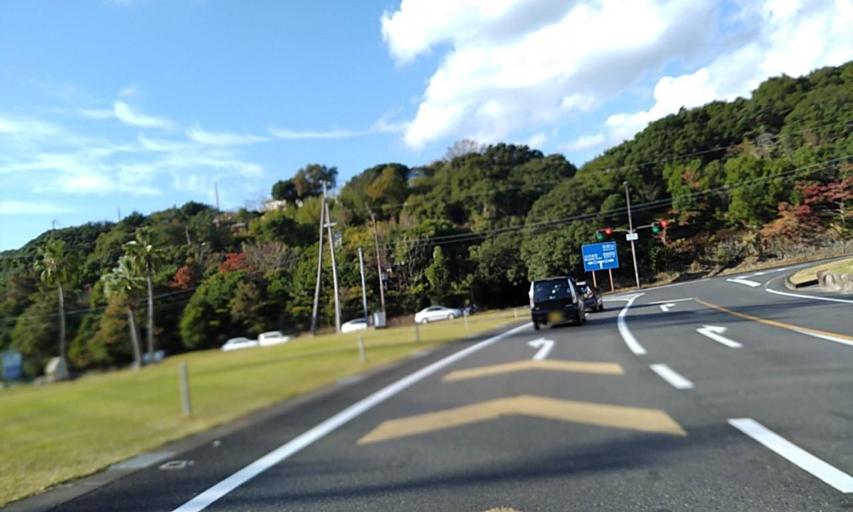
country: JP
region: Wakayama
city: Tanabe
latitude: 33.6791
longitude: 135.3711
